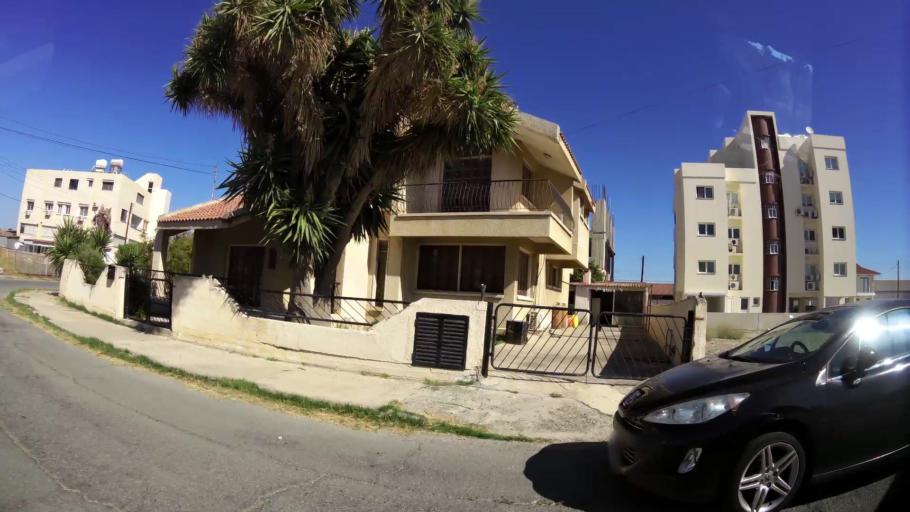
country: CY
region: Larnaka
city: Larnaca
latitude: 34.9339
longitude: 33.6327
